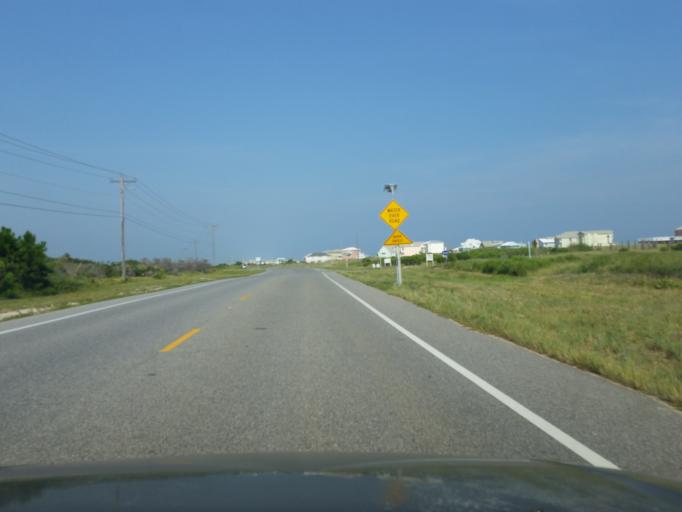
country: US
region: Alabama
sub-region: Mobile County
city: Dauphin Island
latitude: 30.2335
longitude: -87.9533
